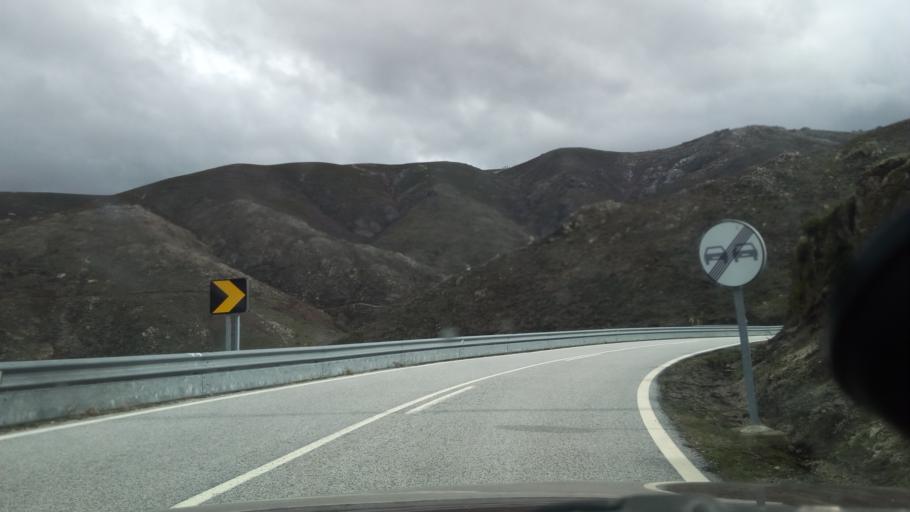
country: PT
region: Guarda
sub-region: Manteigas
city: Manteigas
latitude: 40.4546
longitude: -7.5934
